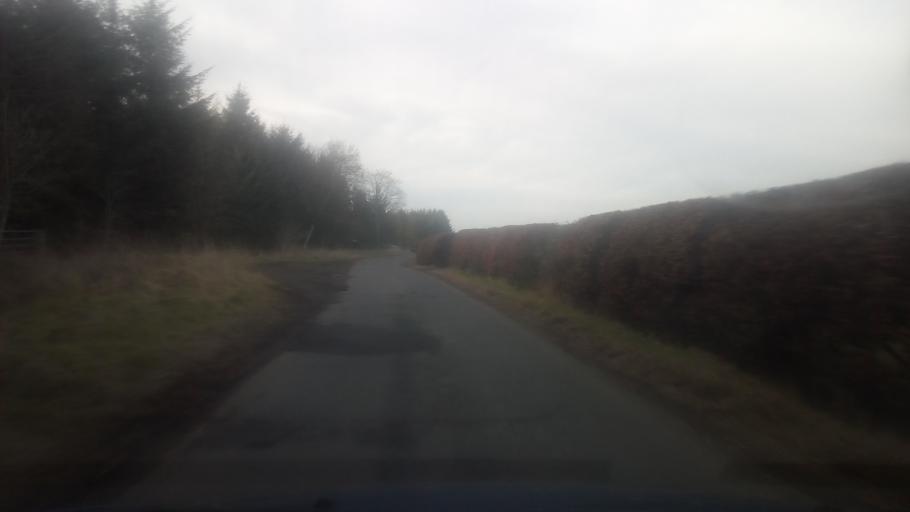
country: GB
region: Scotland
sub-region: The Scottish Borders
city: Jedburgh
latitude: 55.4159
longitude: -2.6178
